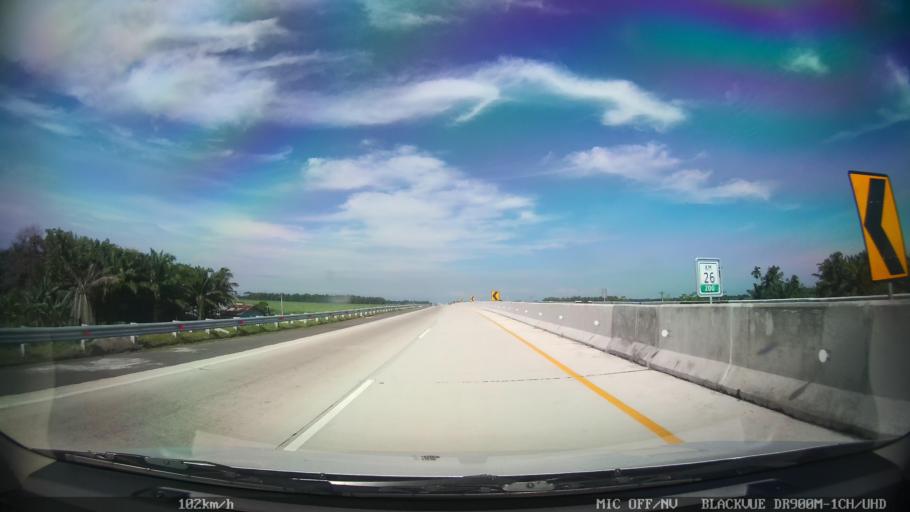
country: ID
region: North Sumatra
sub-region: Kabupaten Langkat
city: Stabat
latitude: 3.7136
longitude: 98.5252
